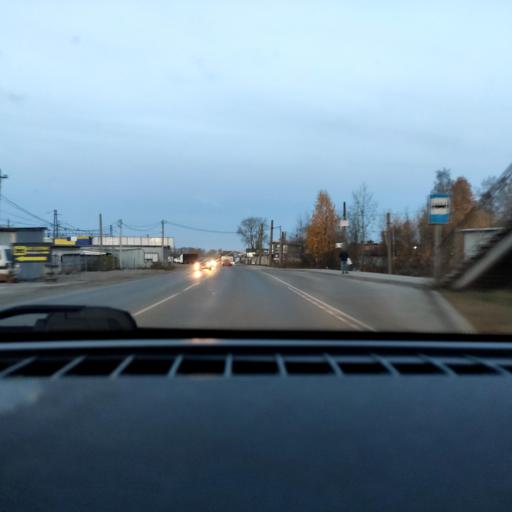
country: RU
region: Perm
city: Froly
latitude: 57.9539
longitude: 56.2358
